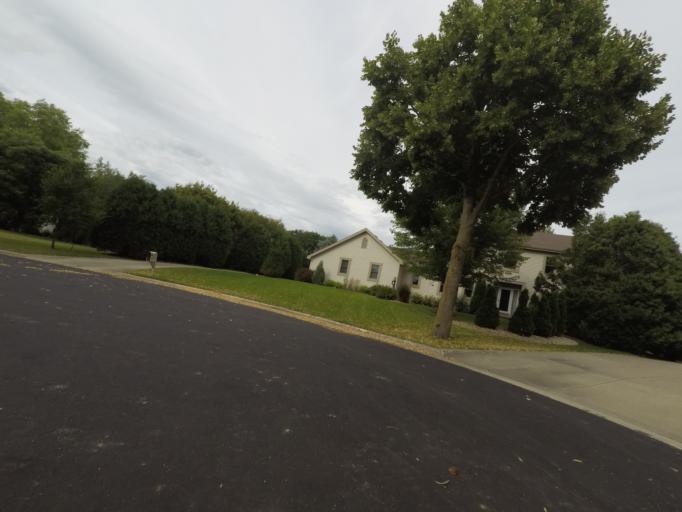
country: US
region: Wisconsin
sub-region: Dane County
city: Middleton
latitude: 43.0830
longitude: -89.4995
